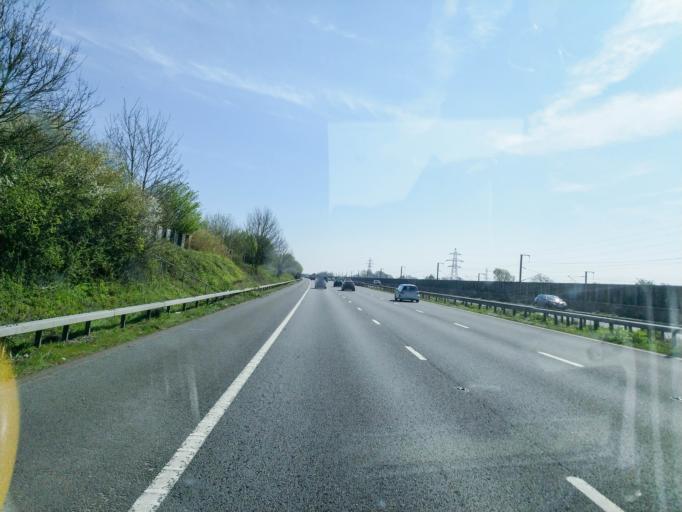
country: GB
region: England
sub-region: Kent
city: Dymchurch
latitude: 51.1020
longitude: 0.9965
